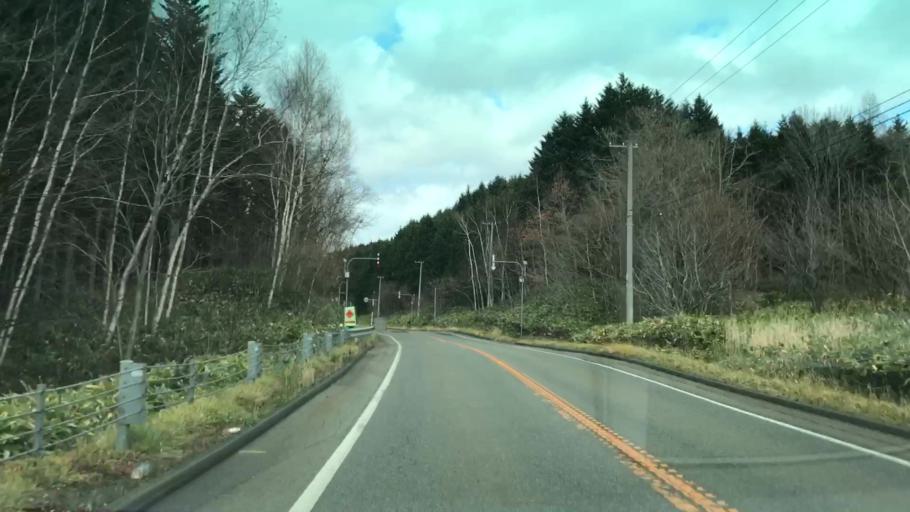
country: JP
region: Hokkaido
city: Shimo-furano
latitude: 42.8941
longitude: 142.4358
